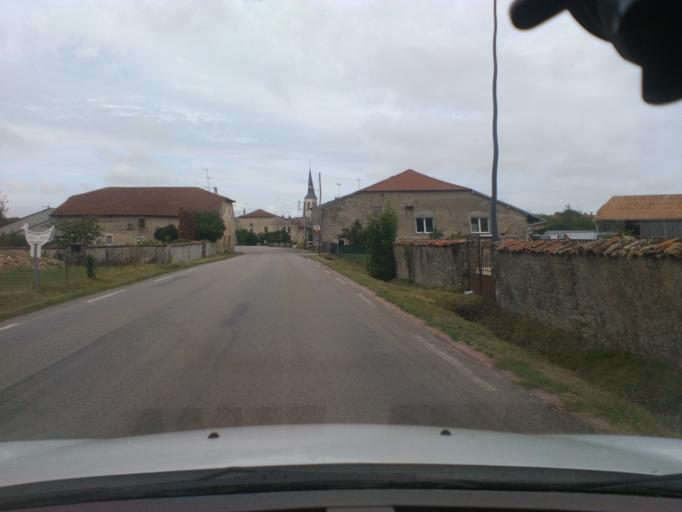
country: FR
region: Lorraine
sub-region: Departement de Meurthe-et-Moselle
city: Vezelise
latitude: 48.4170
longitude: 6.1348
